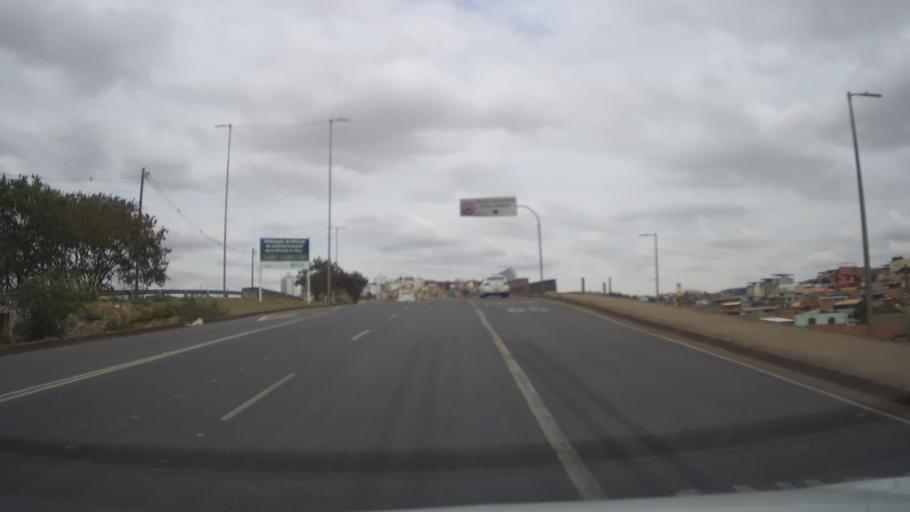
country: BR
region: Minas Gerais
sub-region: Belo Horizonte
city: Belo Horizonte
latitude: -19.8612
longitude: -43.9260
